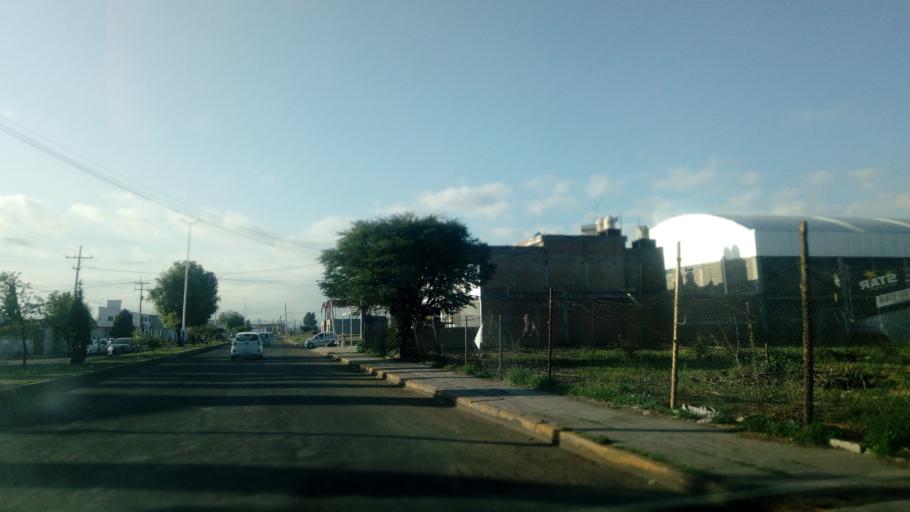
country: MX
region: Durango
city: Victoria de Durango
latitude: 24.0404
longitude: -104.6098
